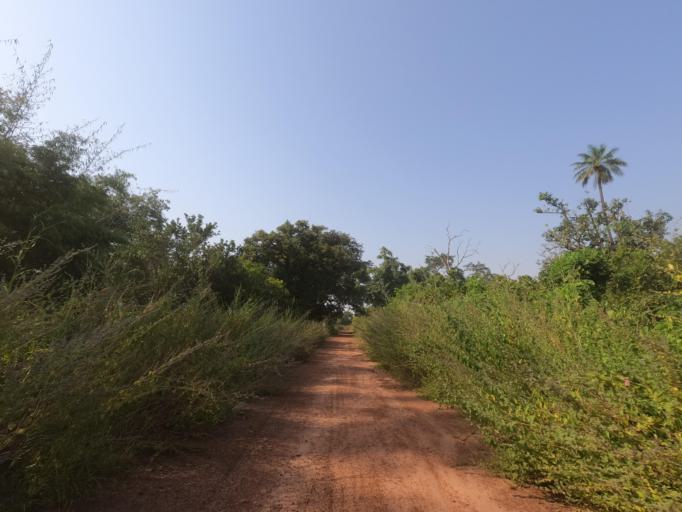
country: SN
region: Sedhiou
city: Sedhiou
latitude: 12.4406
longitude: -15.7379
